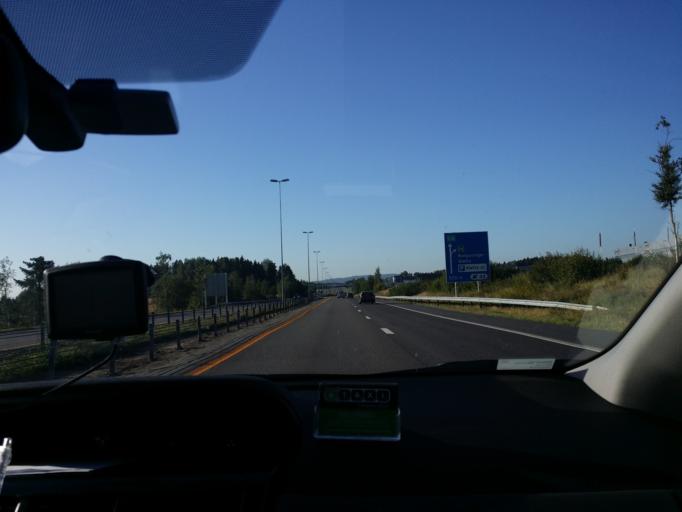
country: NO
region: Akershus
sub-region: Ullensaker
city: Klofta
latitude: 60.0897
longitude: 11.1465
